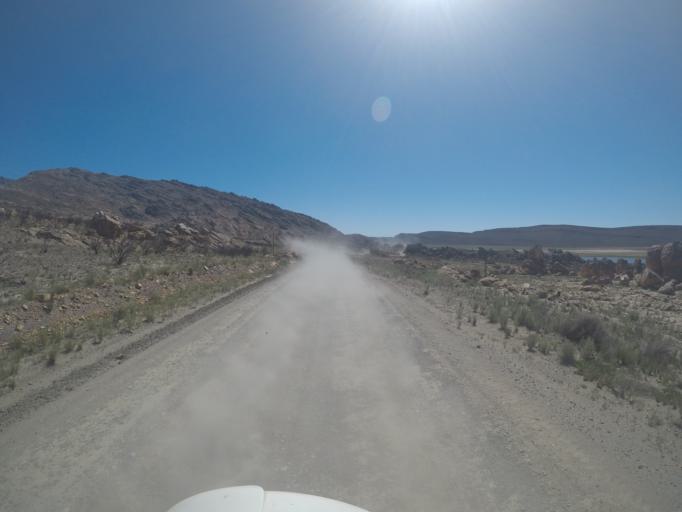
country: ZA
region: Western Cape
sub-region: Cape Winelands District Municipality
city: Ceres
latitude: -32.8503
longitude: 19.4456
